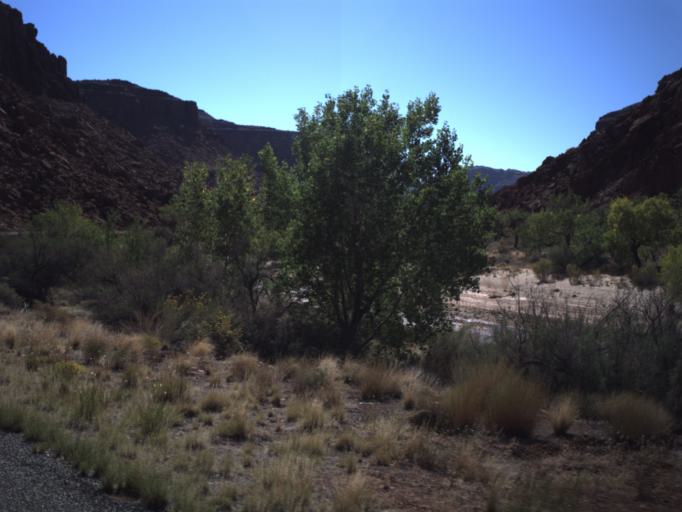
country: US
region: Utah
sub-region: San Juan County
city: Blanding
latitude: 37.9456
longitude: -110.4730
